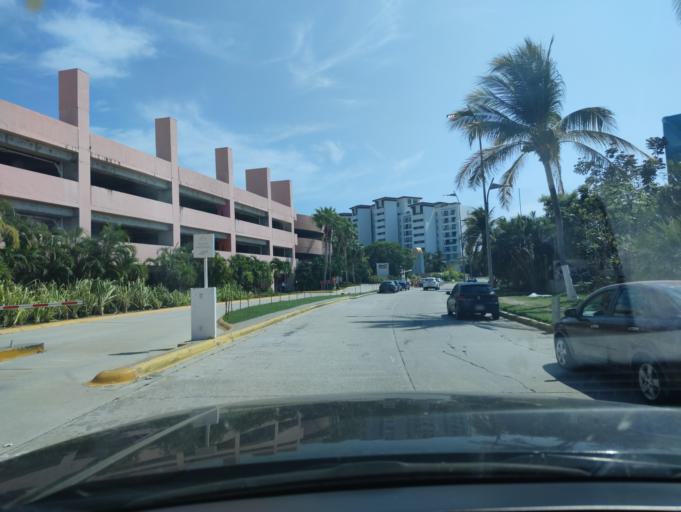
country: MX
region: Guerrero
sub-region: Acapulco de Juarez
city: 10 de Abril
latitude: 16.7724
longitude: -99.7773
